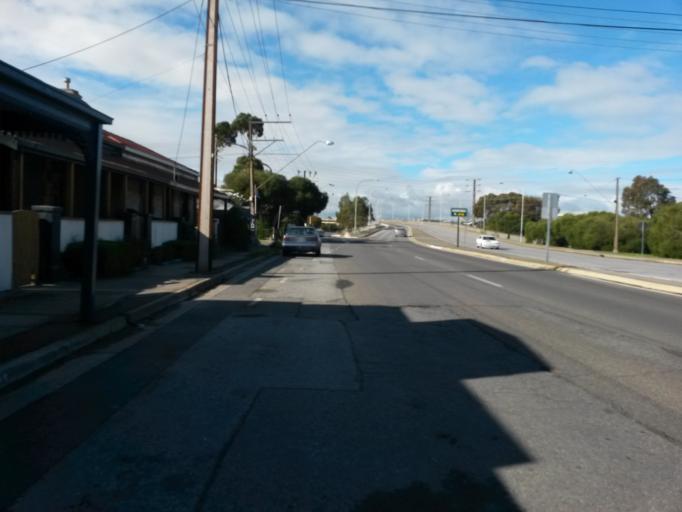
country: AU
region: South Australia
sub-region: Port Adelaide Enfield
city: Birkenhead
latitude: -34.8461
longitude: 138.4918
